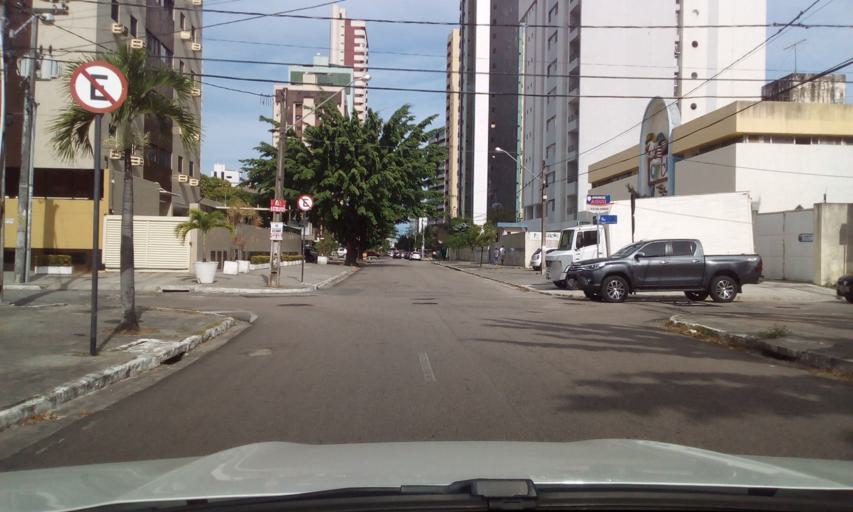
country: BR
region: Paraiba
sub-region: Joao Pessoa
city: Joao Pessoa
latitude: -7.0996
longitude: -34.8402
